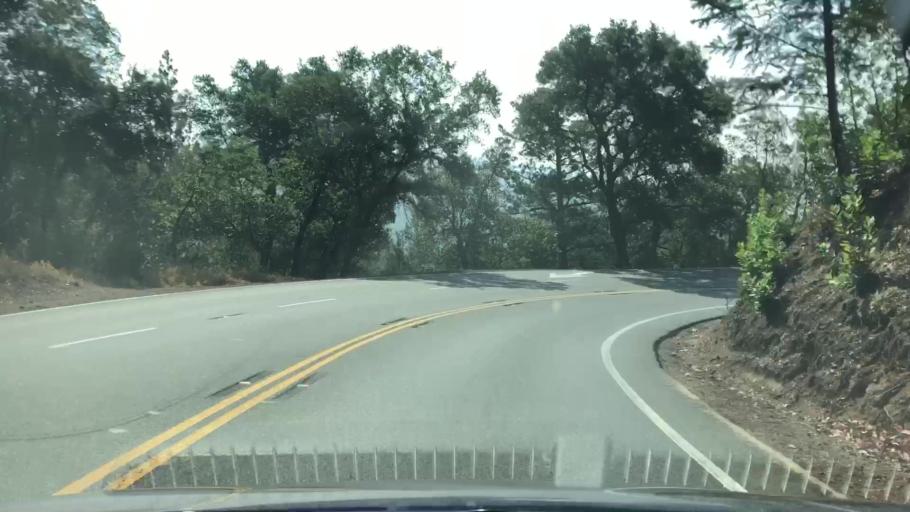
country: US
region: California
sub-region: Napa County
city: Calistoga
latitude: 38.6142
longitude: -122.5966
